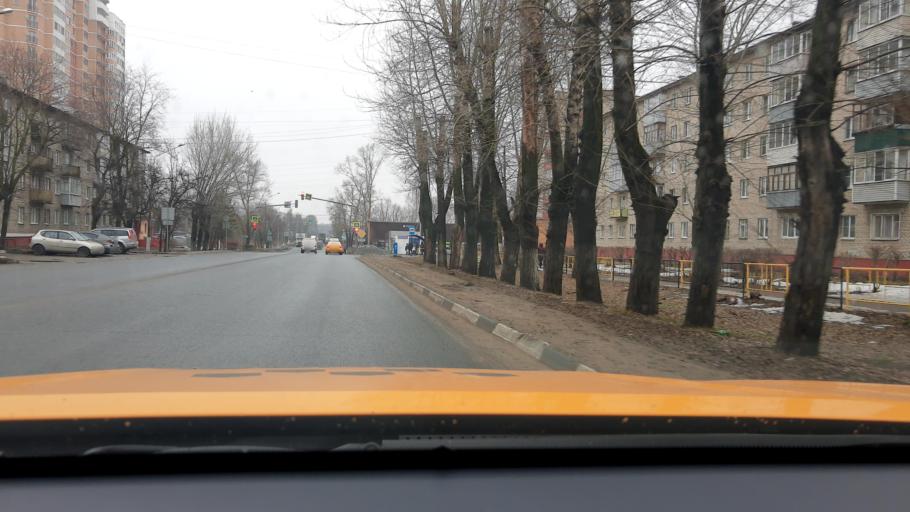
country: RU
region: Moskovskaya
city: Noginsk
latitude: 55.8781
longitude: 38.4303
